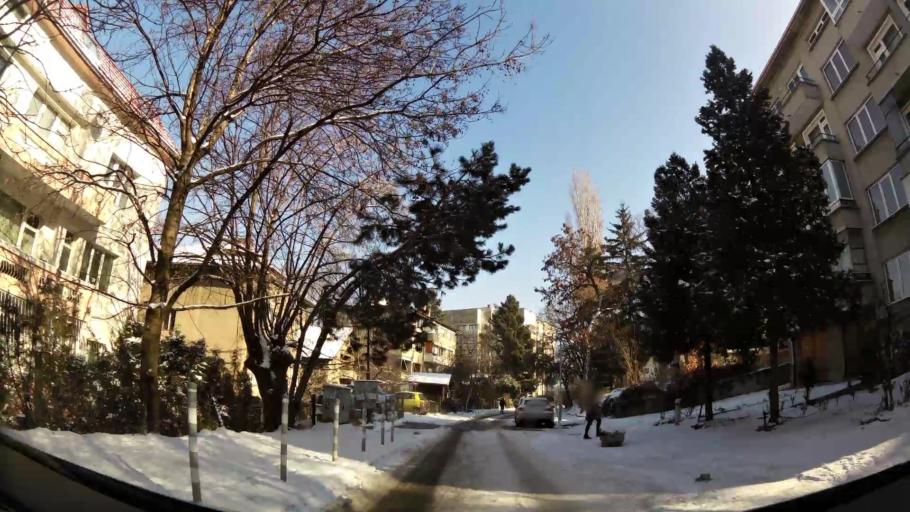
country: BG
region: Sofia-Capital
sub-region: Stolichna Obshtina
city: Sofia
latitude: 42.6739
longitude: 23.3195
